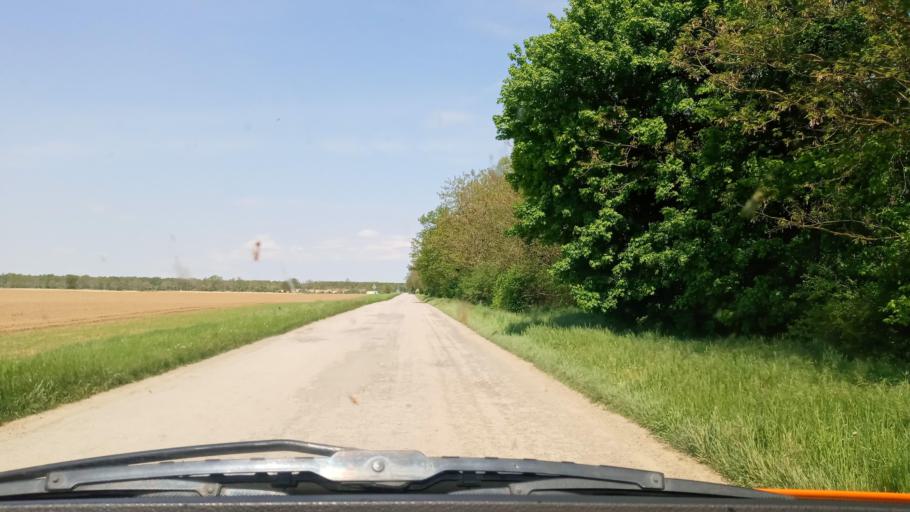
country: HU
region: Baranya
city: Boly
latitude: 45.8828
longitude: 18.5708
